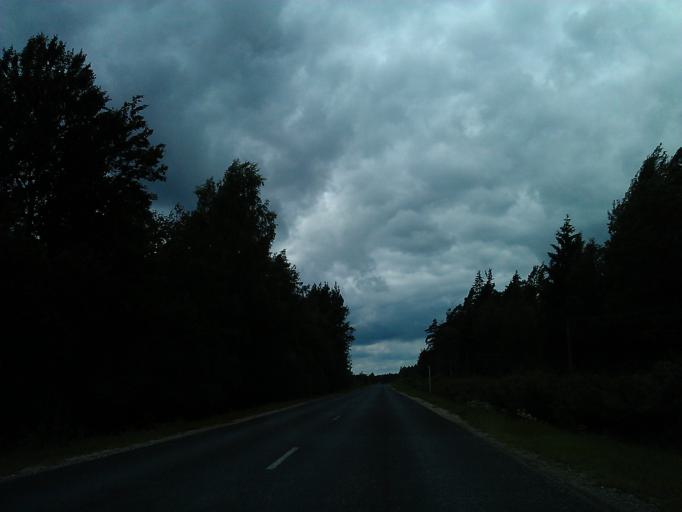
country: LV
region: Talsu Rajons
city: Stende
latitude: 57.0919
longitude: 22.3733
